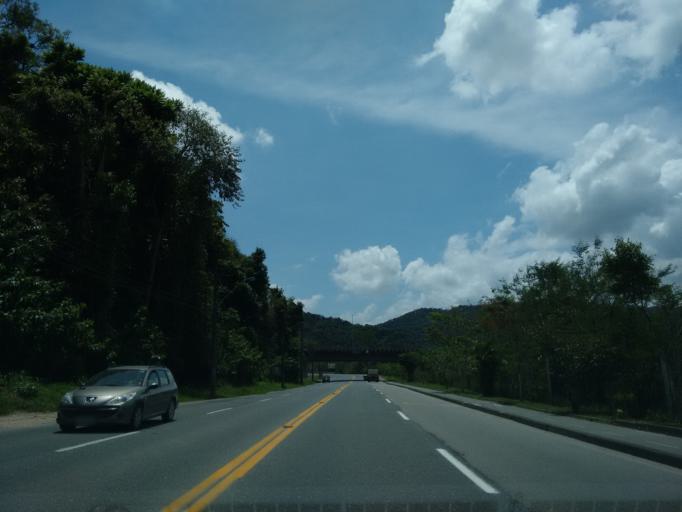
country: BR
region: Santa Catarina
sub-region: Blumenau
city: Blumenau
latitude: -26.9027
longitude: -49.0461
